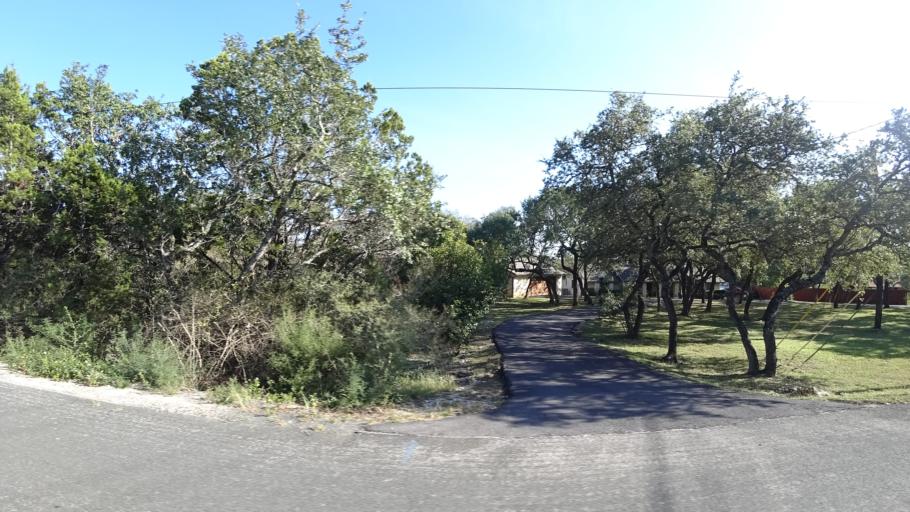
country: US
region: Texas
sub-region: Travis County
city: Barton Creek
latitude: 30.2371
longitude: -97.9230
